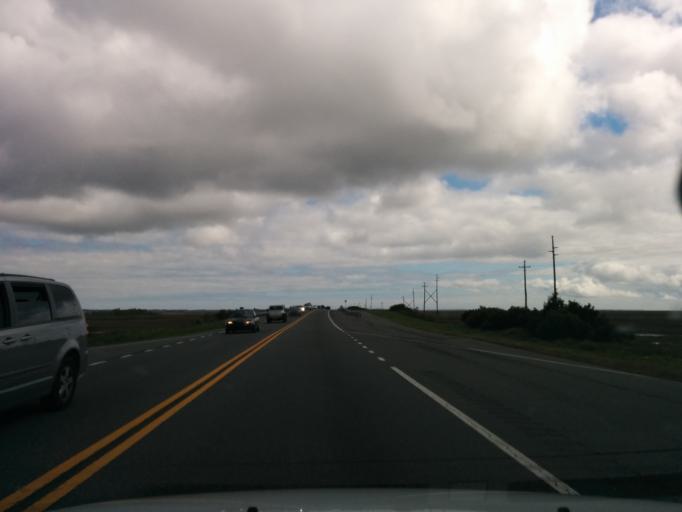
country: US
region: Georgia
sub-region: Glynn County
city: Brunswick
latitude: 31.0904
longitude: -81.4811
